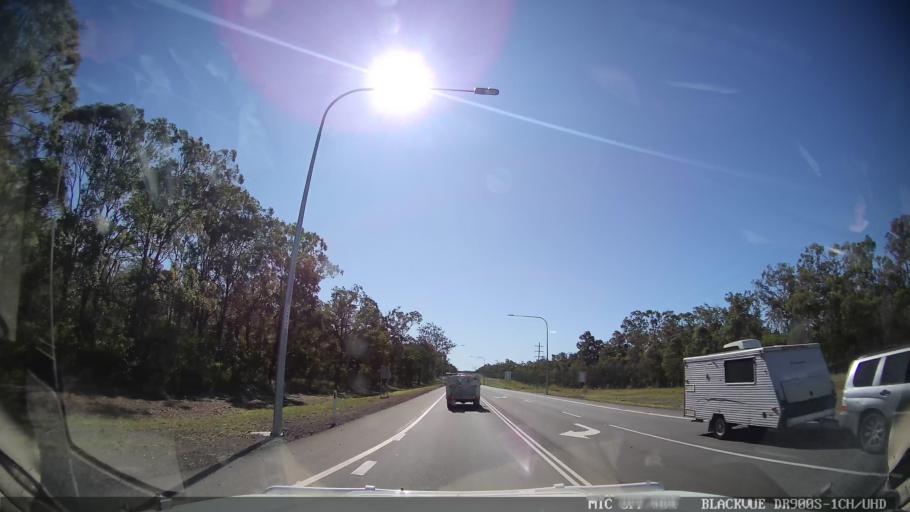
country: AU
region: Queensland
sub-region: Fraser Coast
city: Maryborough
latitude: -25.5108
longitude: 152.6700
